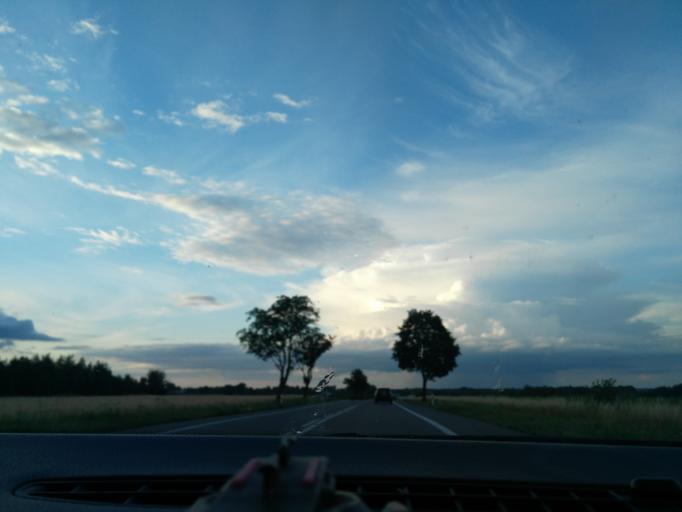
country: PL
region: Lublin Voivodeship
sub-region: Powiat lubartowski
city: Serniki
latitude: 51.4097
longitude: 22.6392
